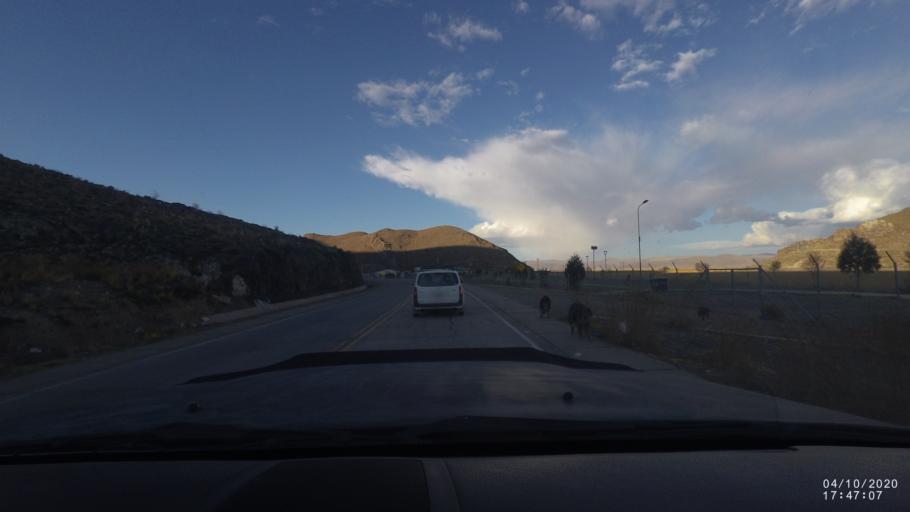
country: BO
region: Oruro
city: Oruro
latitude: -18.0258
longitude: -67.1458
